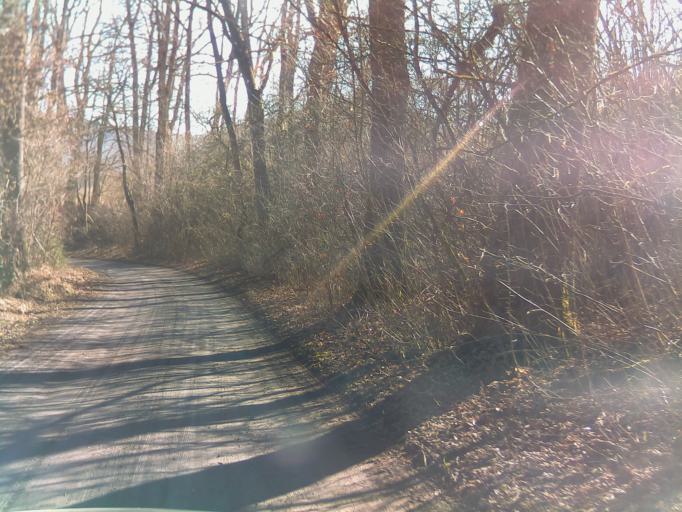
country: DE
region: Thuringia
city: Belrieth
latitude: 50.5403
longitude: 10.4994
